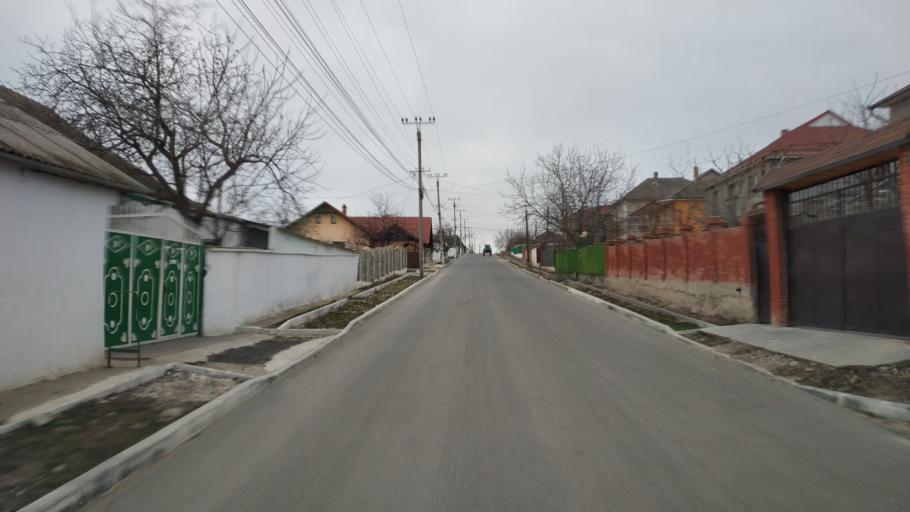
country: MD
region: Laloveni
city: Ialoveni
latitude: 46.9075
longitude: 28.8002
